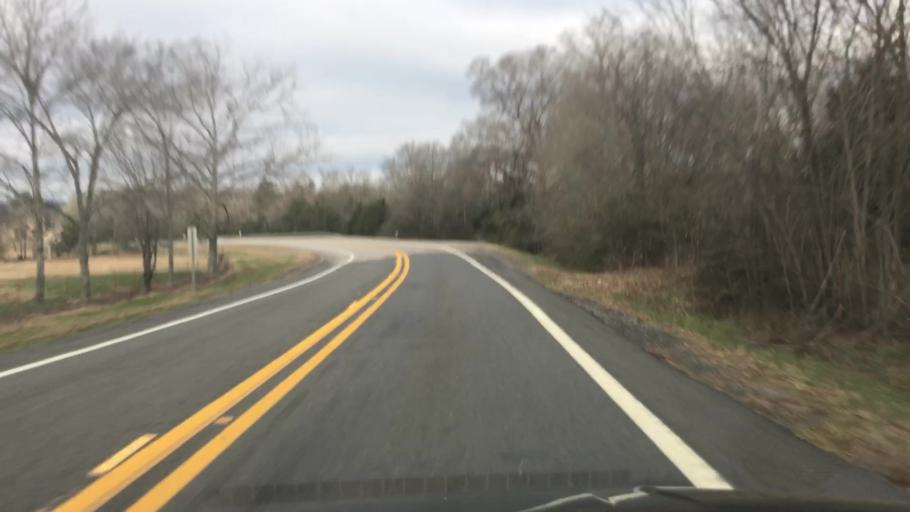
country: US
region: Arkansas
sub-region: Montgomery County
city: Mount Ida
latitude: 34.6582
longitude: -93.7616
